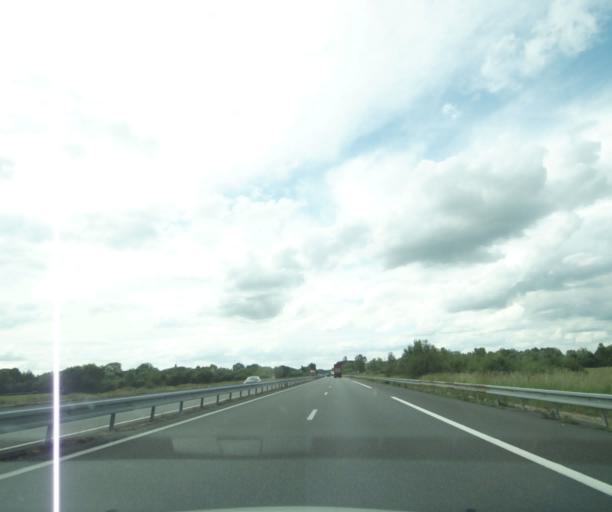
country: FR
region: Centre
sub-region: Departement du Cher
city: Vignoux-sur-Barangeon
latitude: 47.1958
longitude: 2.1514
